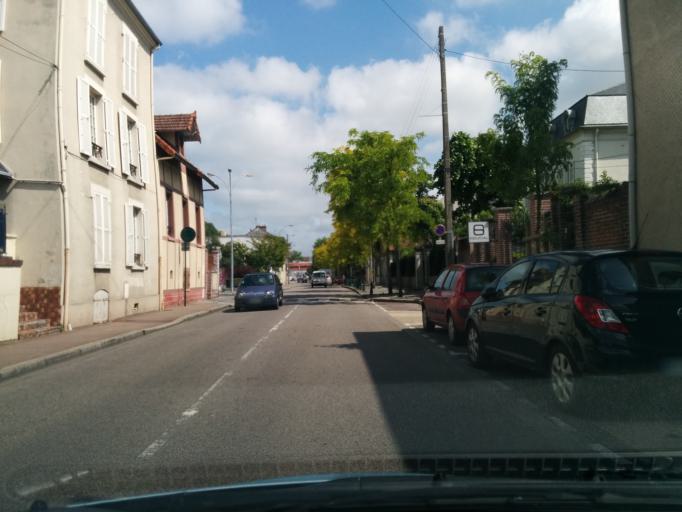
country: FR
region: Ile-de-France
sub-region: Departement des Yvelines
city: Mantes-la-Jolie
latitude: 48.9801
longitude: 1.7154
